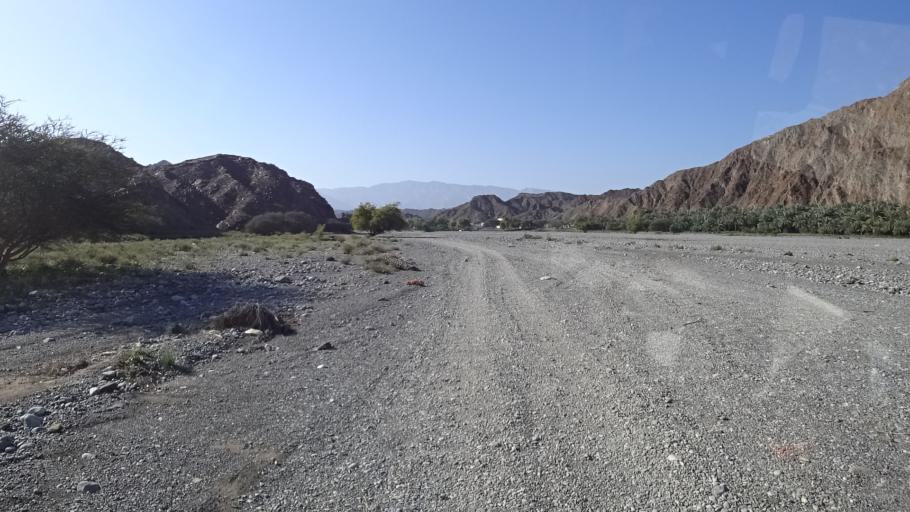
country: OM
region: Al Batinah
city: Bayt al `Awabi
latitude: 23.3988
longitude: 57.6640
